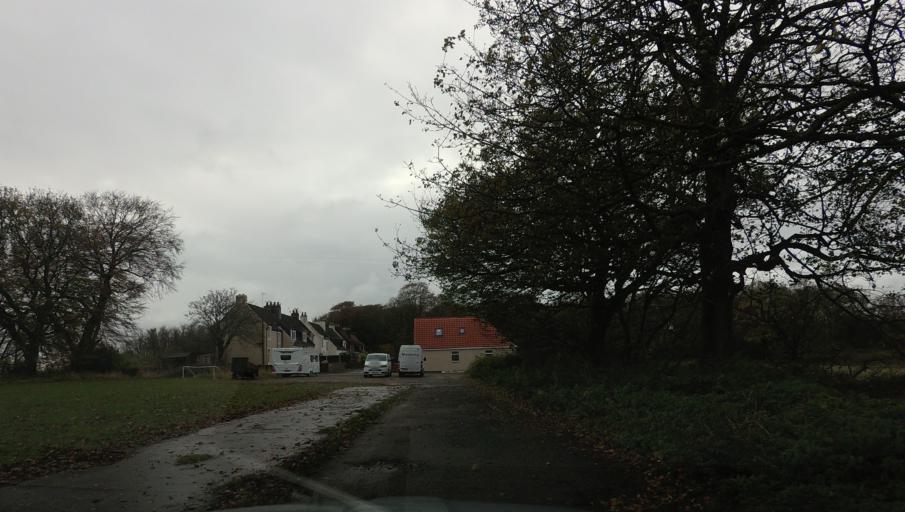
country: GB
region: Scotland
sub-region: Fife
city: East Wemyss
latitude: 56.1538
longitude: -3.0726
